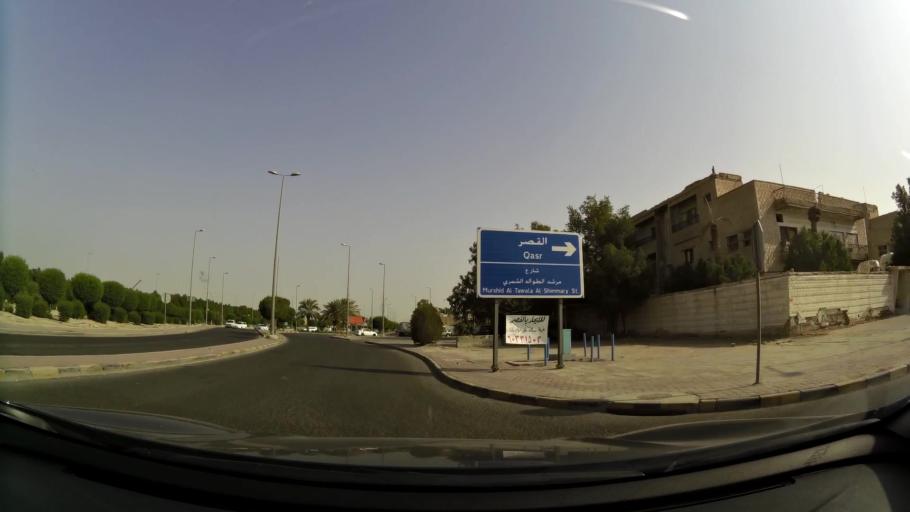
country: KW
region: Muhafazat al Jahra'
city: Al Jahra'
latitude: 29.3478
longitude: 47.6953
